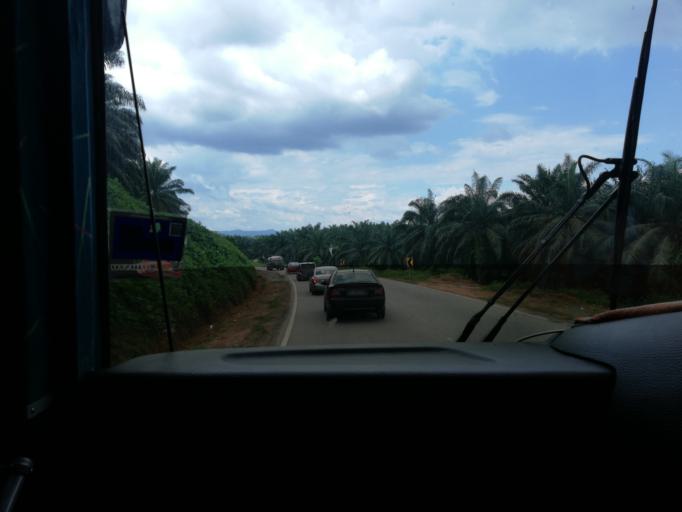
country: MY
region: Perak
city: Parit Buntar
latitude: 5.1713
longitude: 100.5989
